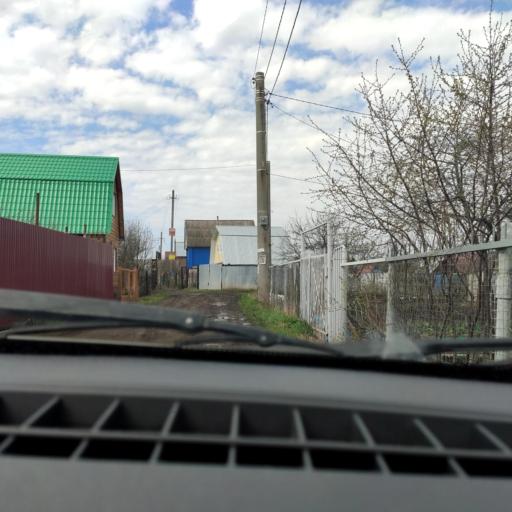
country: RU
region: Bashkortostan
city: Avdon
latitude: 54.7202
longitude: 55.7919
